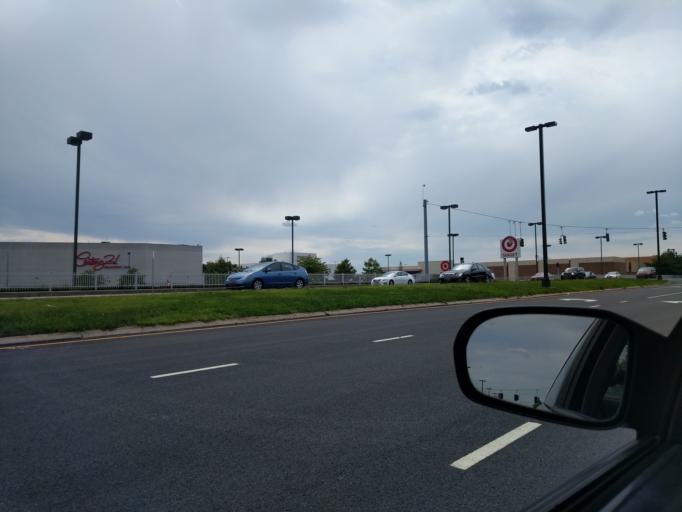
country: US
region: New York
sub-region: Nassau County
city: South Valley Stream
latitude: 40.6647
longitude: -73.7177
